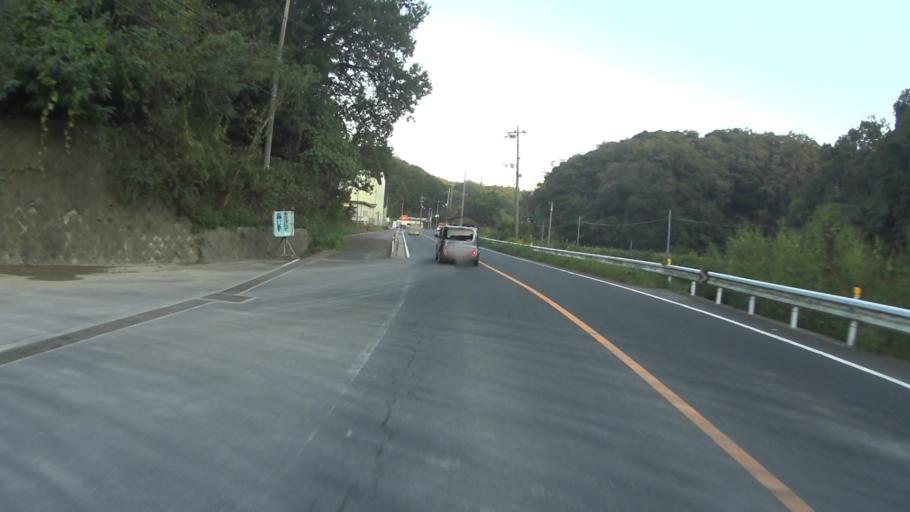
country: JP
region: Kyoto
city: Miyazu
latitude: 35.6502
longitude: 135.0381
